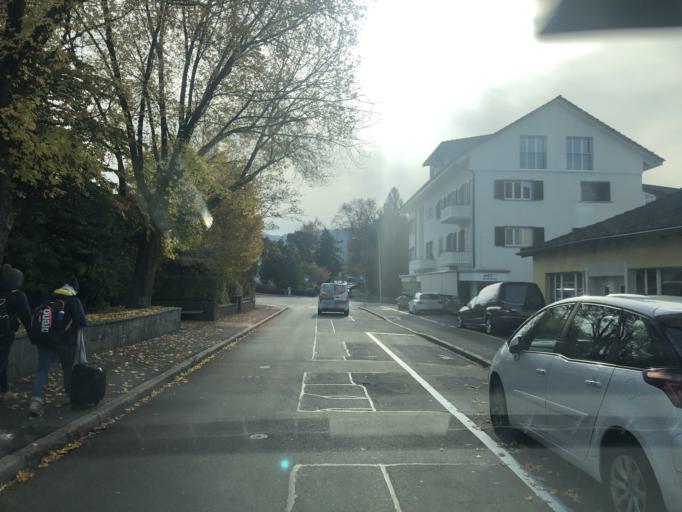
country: CH
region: Aargau
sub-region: Bezirk Baden
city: Wettingen
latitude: 47.4629
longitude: 8.3185
